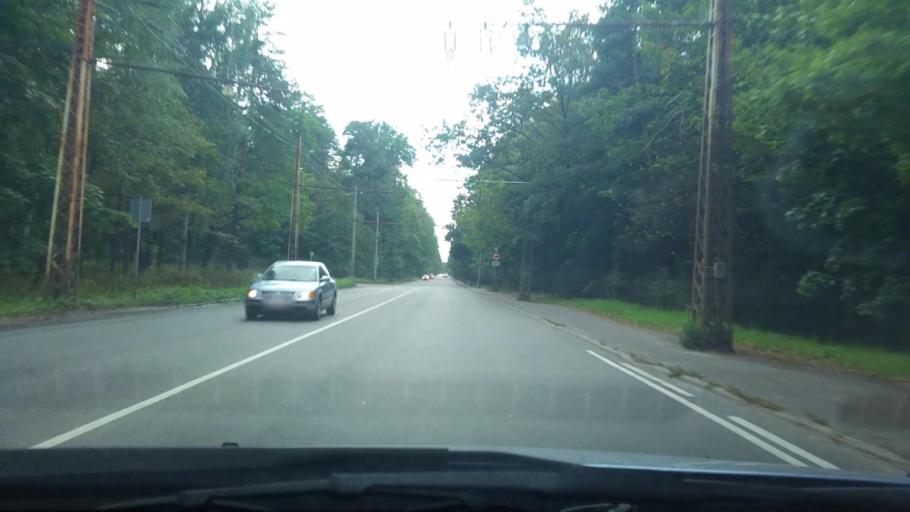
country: LV
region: Stopini
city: Ulbroka
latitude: 56.9601
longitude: 24.2283
